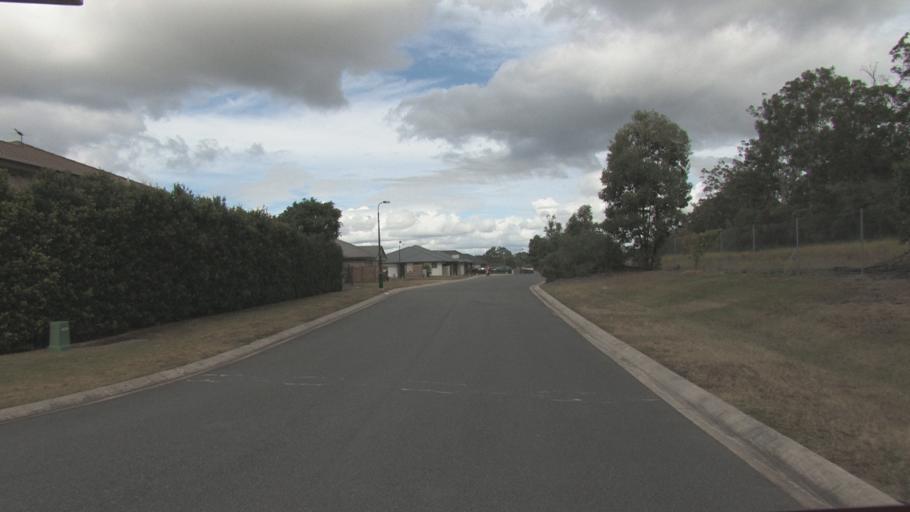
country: AU
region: Queensland
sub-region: Logan
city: Park Ridge South
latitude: -27.6691
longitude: 153.0211
